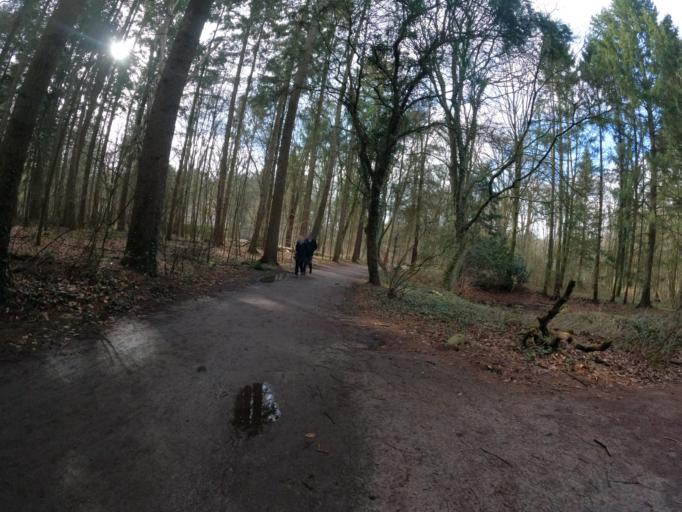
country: DE
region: Hamburg
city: Stellingen
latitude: 53.6158
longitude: 9.9374
